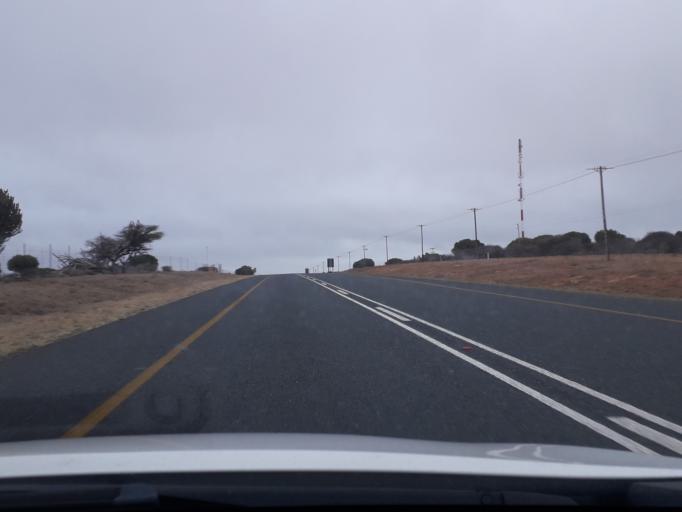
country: ZA
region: Limpopo
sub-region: Vhembe District Municipality
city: Louis Trichardt
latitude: -23.4068
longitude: 29.7570
